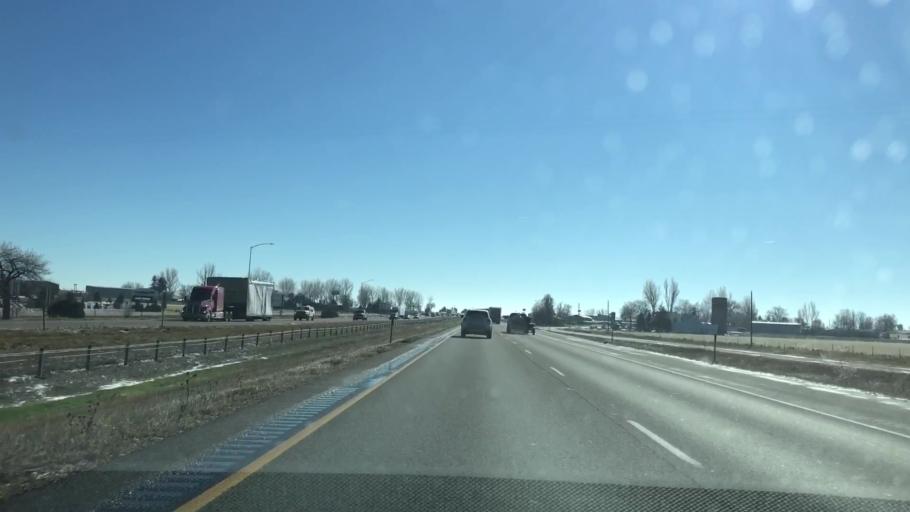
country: US
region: Colorado
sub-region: Weld County
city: Johnstown
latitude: 40.3605
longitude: -104.9844
